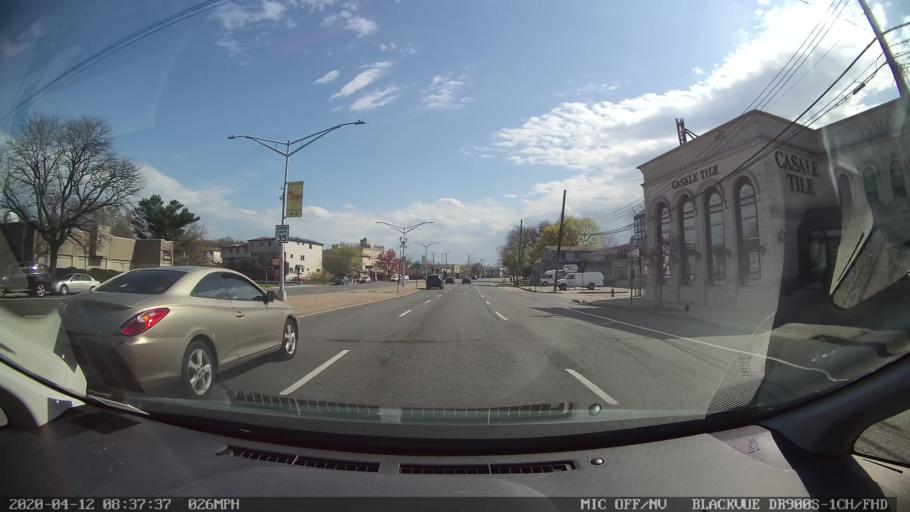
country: US
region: New York
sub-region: Richmond County
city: Bloomfield
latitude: 40.6062
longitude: -74.1626
